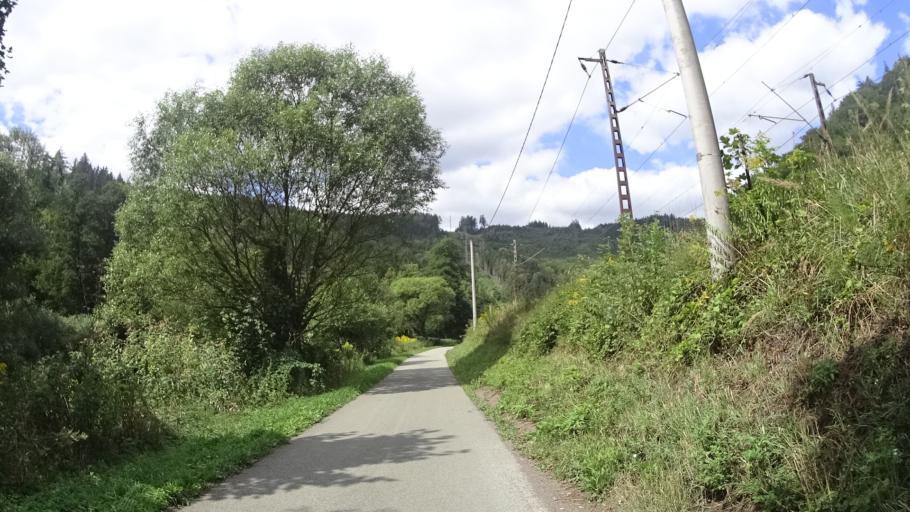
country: CZ
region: Pardubicky
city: Horni Sloupnice
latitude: 49.9741
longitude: 16.3403
